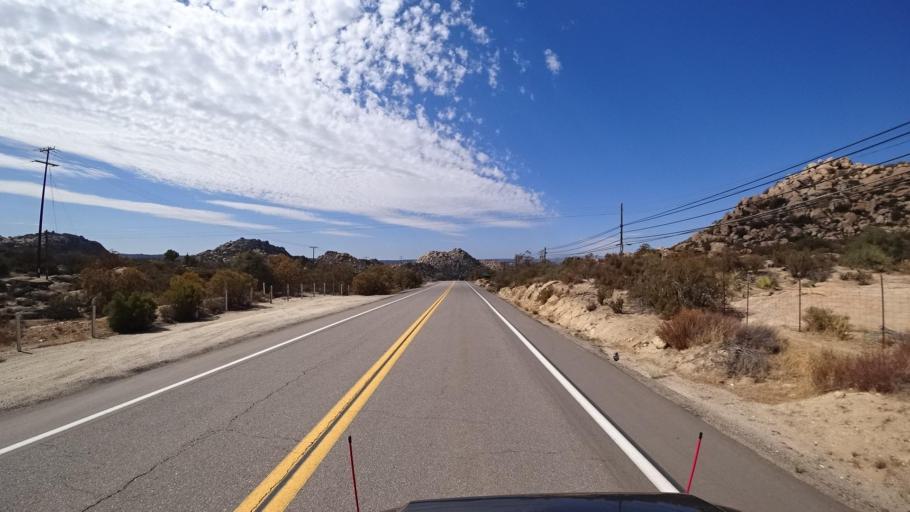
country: MX
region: Baja California
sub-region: Tecate
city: Cereso del Hongo
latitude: 32.6449
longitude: -116.2359
